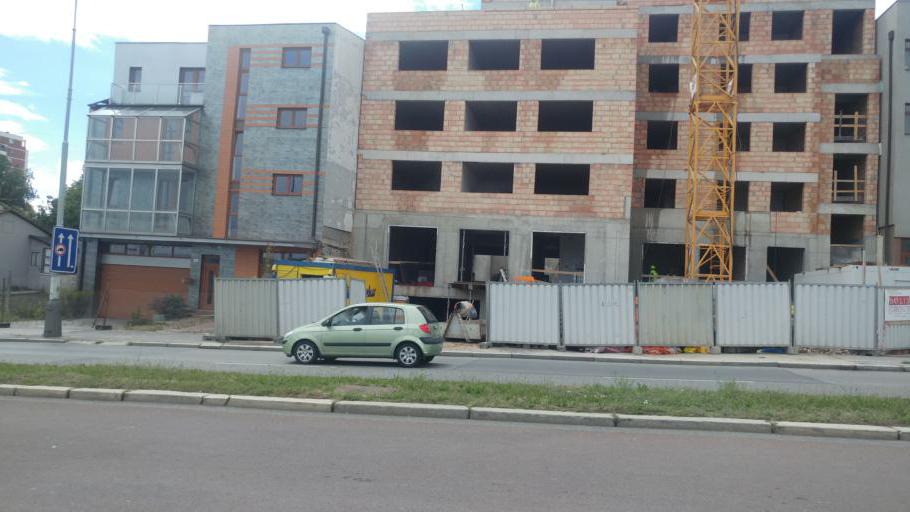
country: CZ
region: Praha
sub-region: Praha 8
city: Karlin
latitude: 50.0601
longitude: 14.4700
